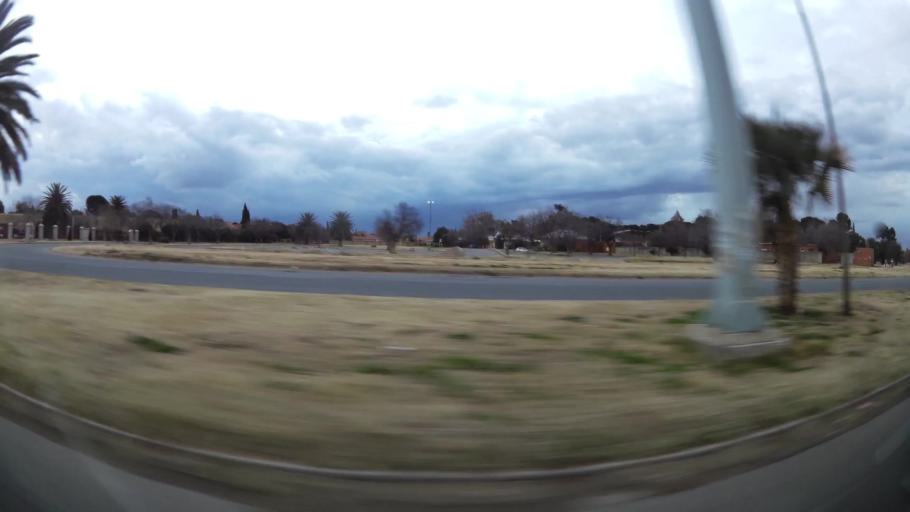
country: ZA
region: Orange Free State
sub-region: Lejweleputswa District Municipality
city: Welkom
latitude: -27.9768
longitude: 26.7329
